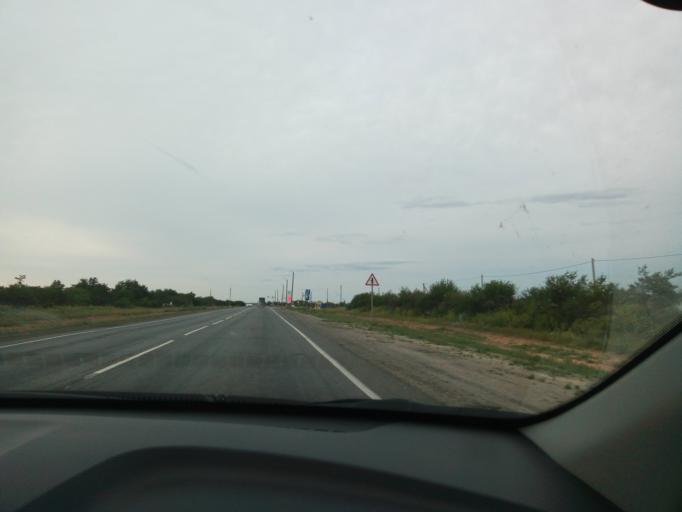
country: RU
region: Volgograd
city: Dubovka
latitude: 49.0410
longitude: 44.7680
